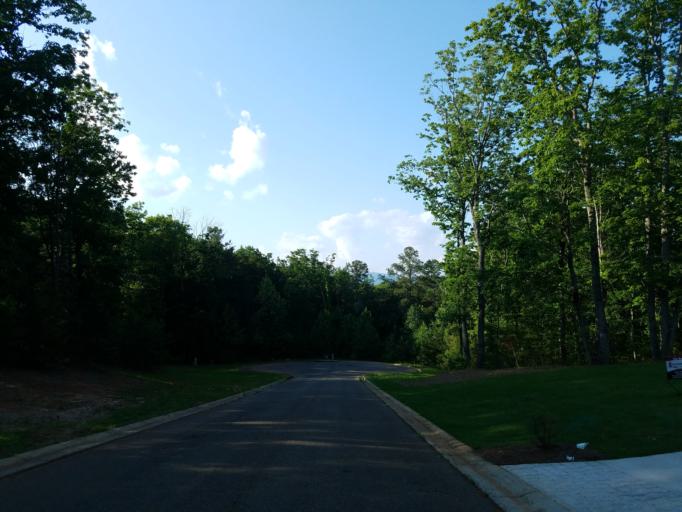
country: US
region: Georgia
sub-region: Pickens County
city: Nelson
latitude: 34.3856
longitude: -84.3233
